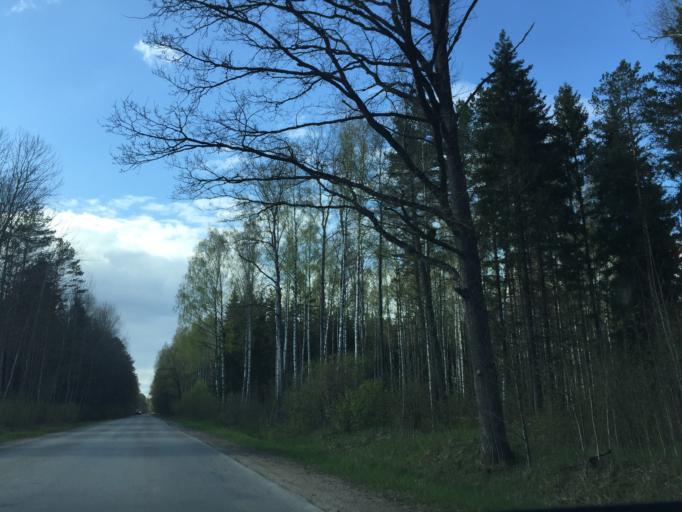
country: LV
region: Jelgava
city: Jelgava
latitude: 56.5686
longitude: 23.7482
